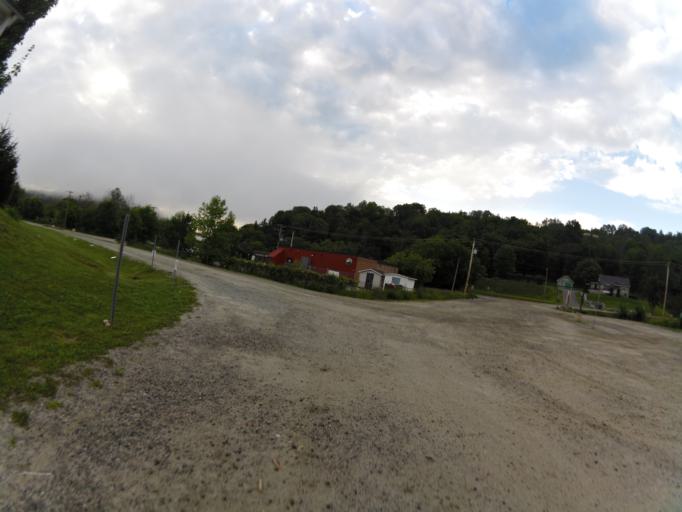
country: CA
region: Quebec
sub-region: Outaouais
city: Wakefield
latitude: 45.6323
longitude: -75.9314
